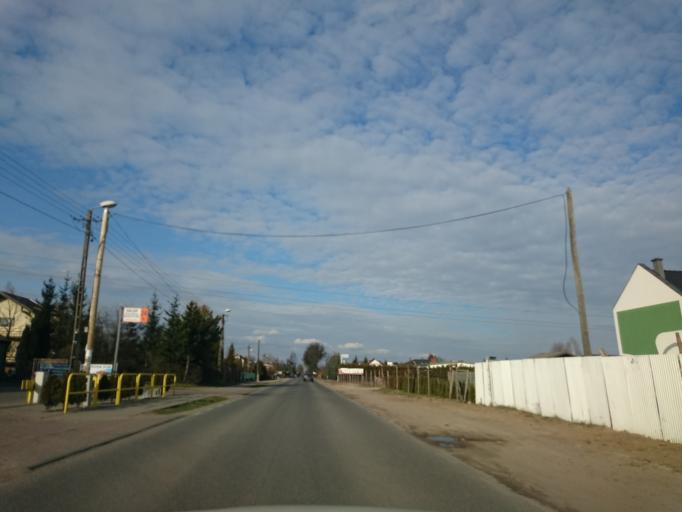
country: PL
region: Kujawsko-Pomorskie
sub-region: Powiat torunski
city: Lubicz Gorny
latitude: 53.0313
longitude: 18.7755
